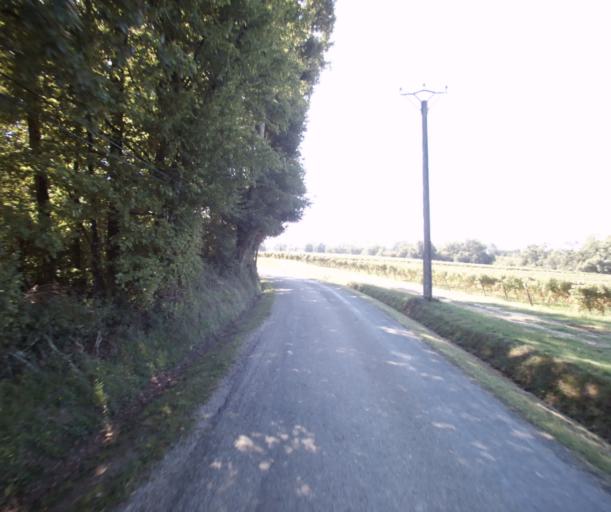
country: FR
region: Midi-Pyrenees
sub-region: Departement du Gers
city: Cazaubon
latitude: 43.9234
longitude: -0.0267
